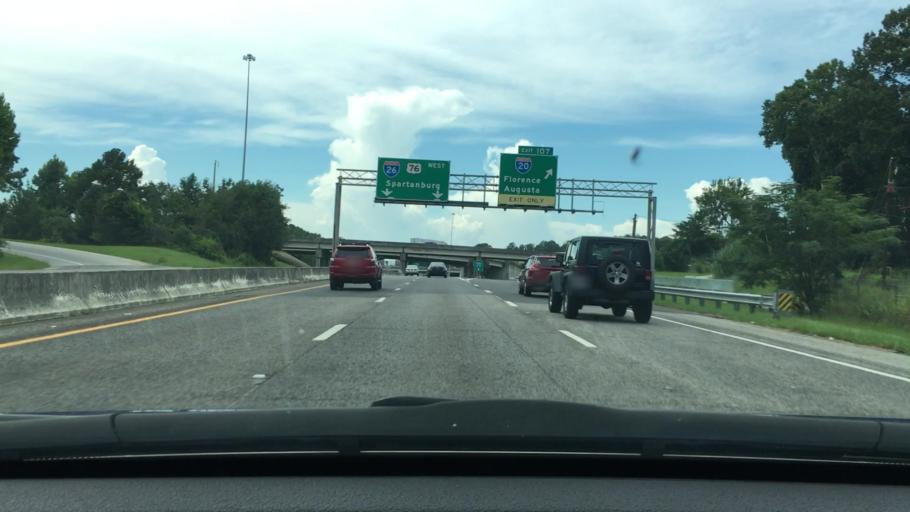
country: US
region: South Carolina
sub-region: Lexington County
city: Saint Andrews
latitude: 34.0264
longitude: -81.0999
